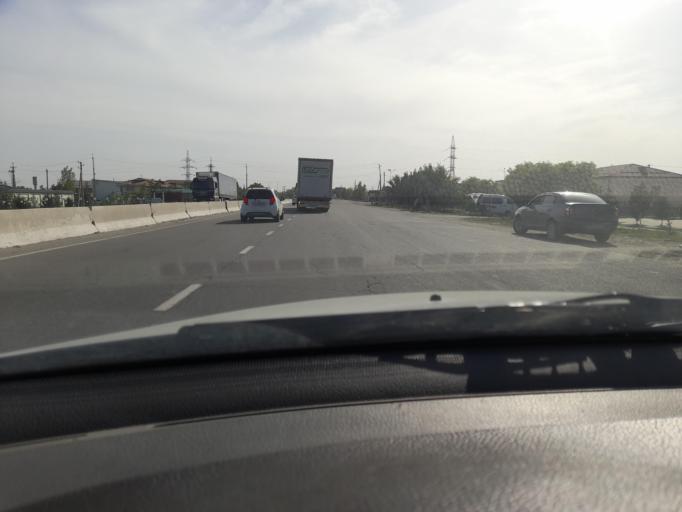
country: UZ
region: Samarqand
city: Kattaqo'rg'on
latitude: 39.9269
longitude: 66.2427
